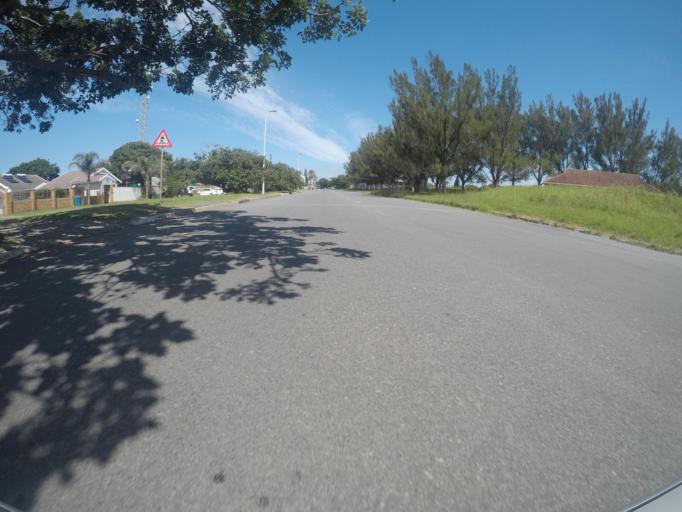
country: ZA
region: Eastern Cape
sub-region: Buffalo City Metropolitan Municipality
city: East London
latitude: -32.9405
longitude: 28.0255
